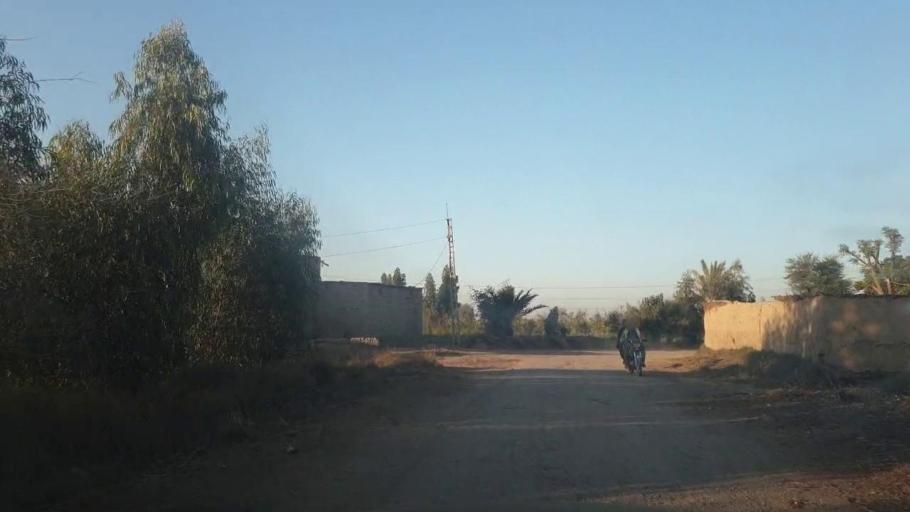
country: PK
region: Sindh
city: Mirpur Mathelo
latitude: 27.9859
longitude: 69.4553
